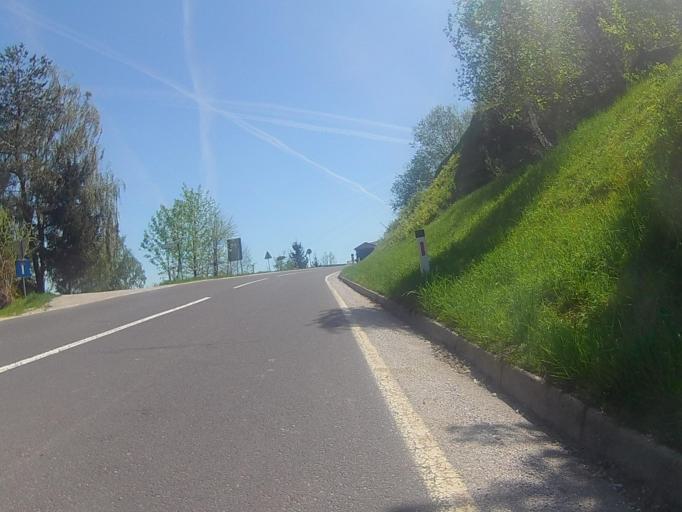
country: SI
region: Maribor
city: Razvanje
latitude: 46.4885
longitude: 15.6026
